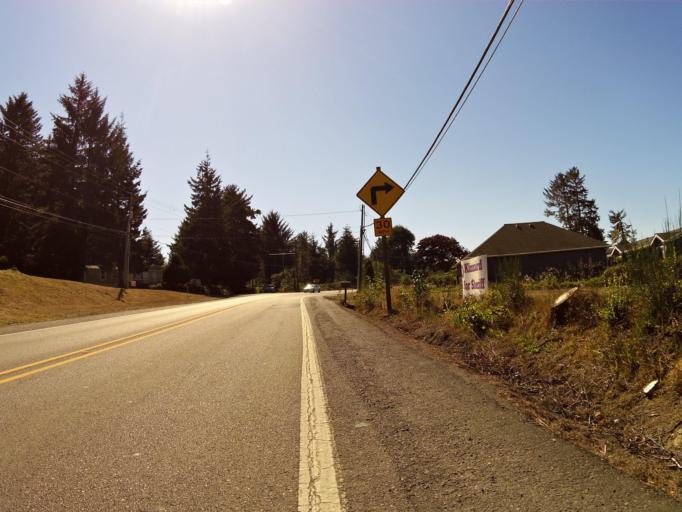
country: US
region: Oregon
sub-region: Coos County
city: Barview
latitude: 43.3432
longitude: -124.3148
